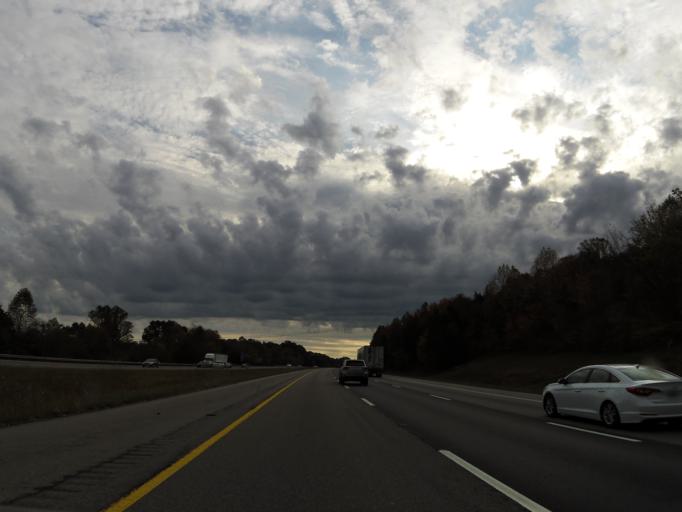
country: US
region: Tennessee
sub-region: Knox County
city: Mascot
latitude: 36.0046
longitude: -83.7453
